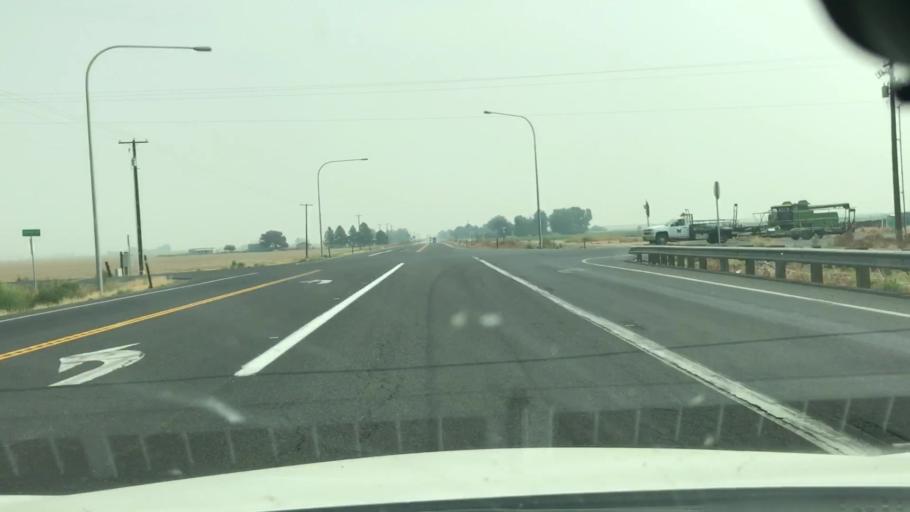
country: US
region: Washington
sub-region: Grant County
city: Quincy
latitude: 47.2342
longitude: -119.7689
